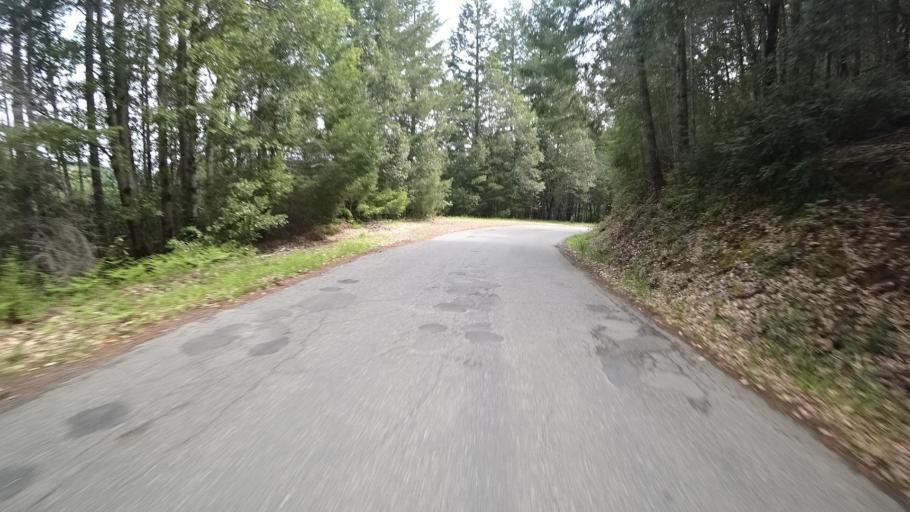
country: US
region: California
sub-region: Humboldt County
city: Redway
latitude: 40.0637
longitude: -123.8319
